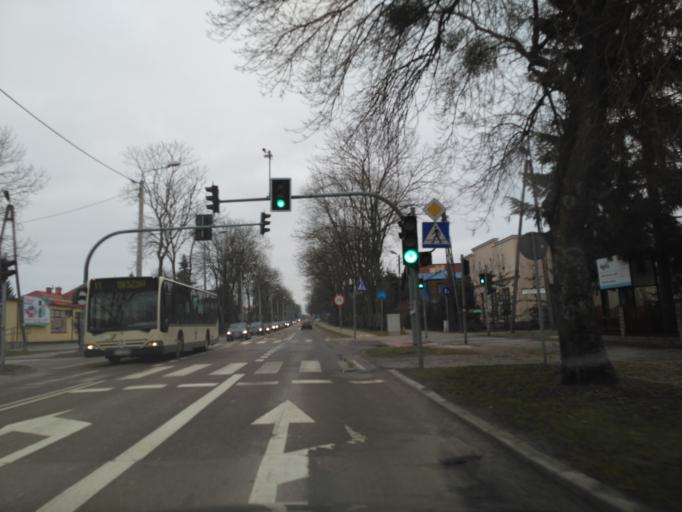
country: PL
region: Lublin Voivodeship
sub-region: Chelm
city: Chelm
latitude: 51.1271
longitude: 23.4895
